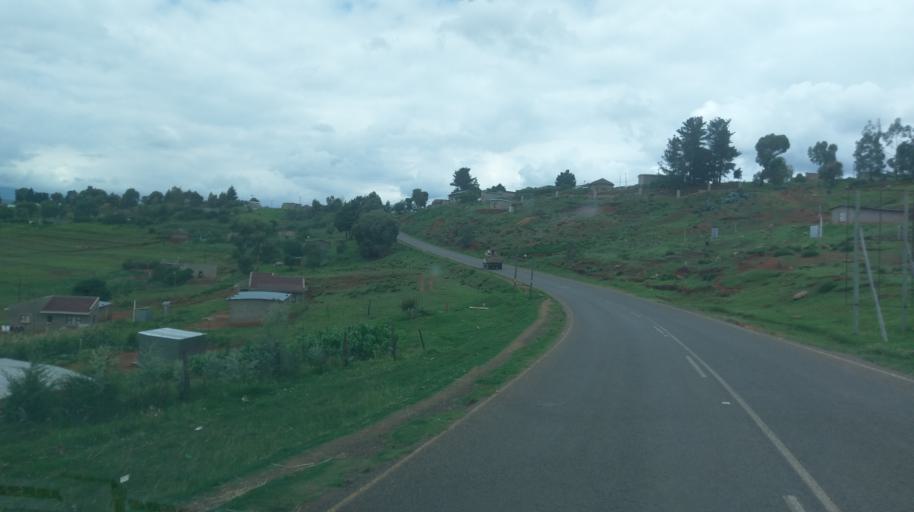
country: LS
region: Leribe
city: Leribe
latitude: -28.9983
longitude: 28.2051
